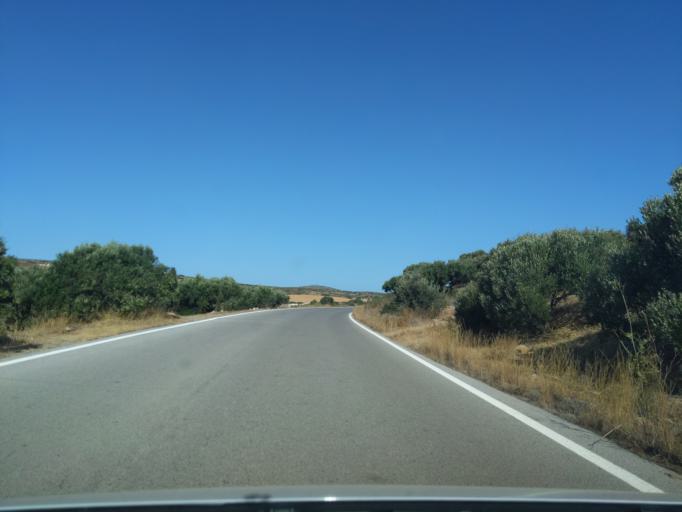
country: GR
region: Crete
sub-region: Nomos Lasithiou
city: Palekastro
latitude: 35.2285
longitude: 26.2555
